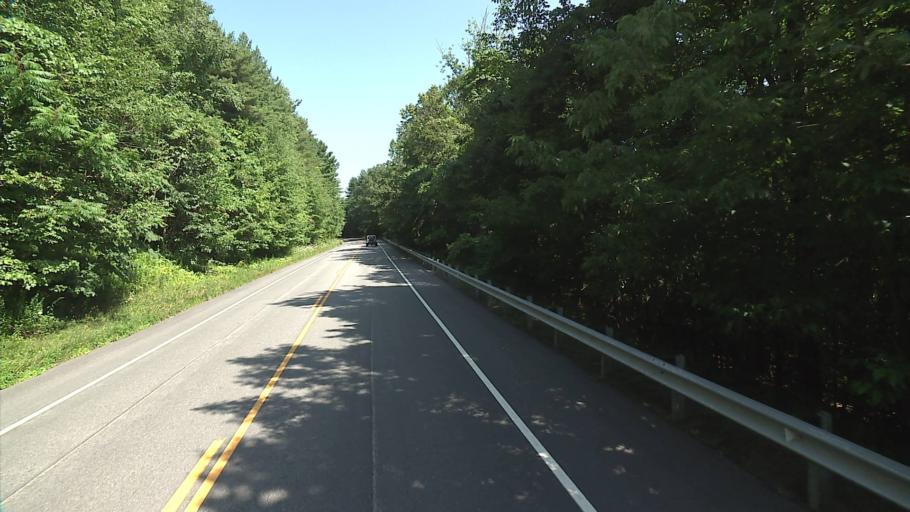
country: US
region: Connecticut
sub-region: Litchfield County
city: Winchester Center
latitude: 41.8813
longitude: -73.1701
